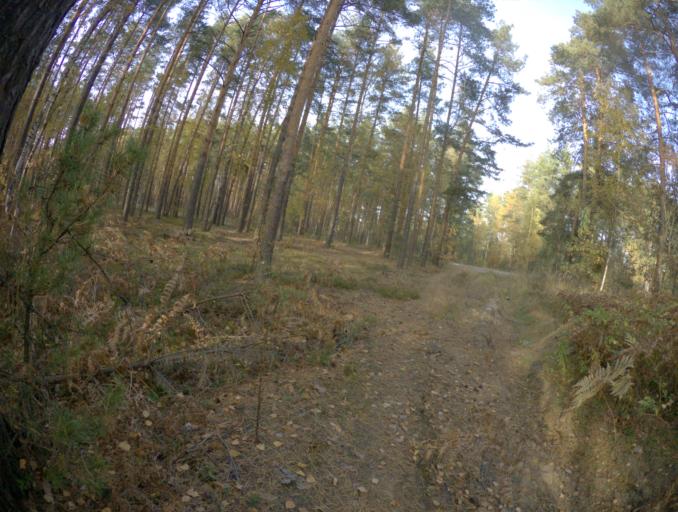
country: RU
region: Vladimir
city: Sobinka
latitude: 55.9927
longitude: 40.0583
